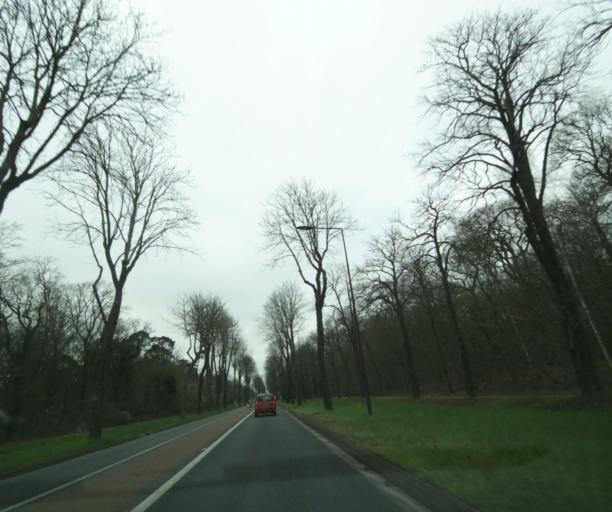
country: FR
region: Ile-de-France
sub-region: Departement des Yvelines
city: Poissy
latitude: 48.9186
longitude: 2.0618
